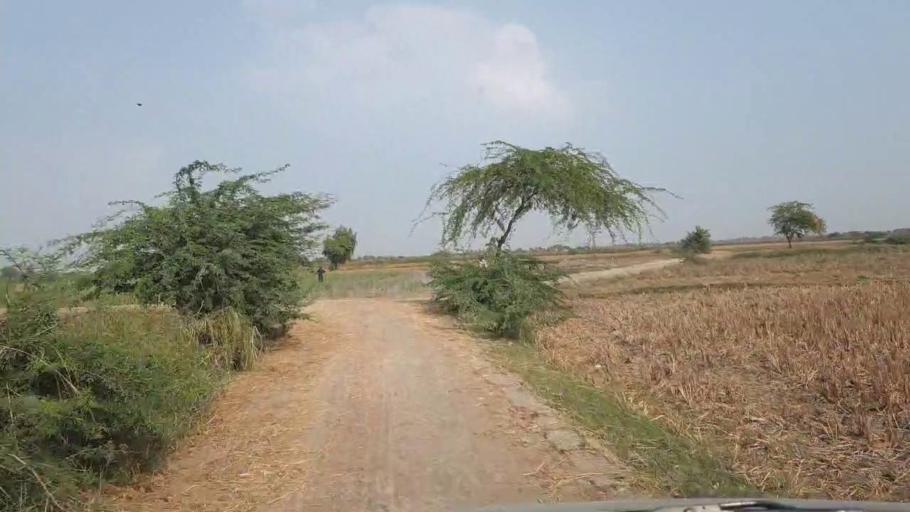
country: PK
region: Sindh
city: Matli
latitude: 24.9830
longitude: 68.7043
